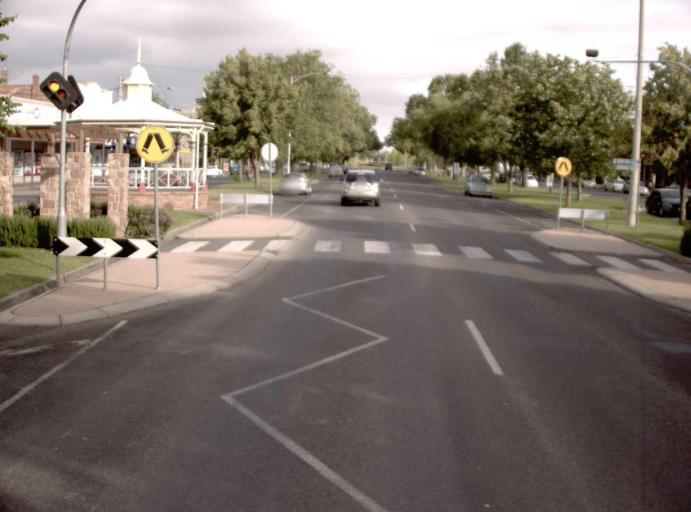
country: AU
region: Victoria
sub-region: Wellington
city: Sale
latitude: -37.9668
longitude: 146.9759
